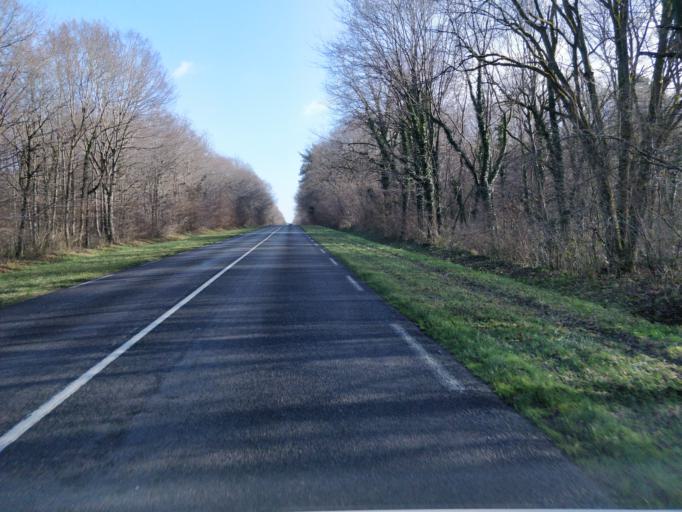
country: FR
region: Ile-de-France
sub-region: Departement de Seine-et-Marne
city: Bagneaux-sur-Loing
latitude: 48.2451
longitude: 2.7831
